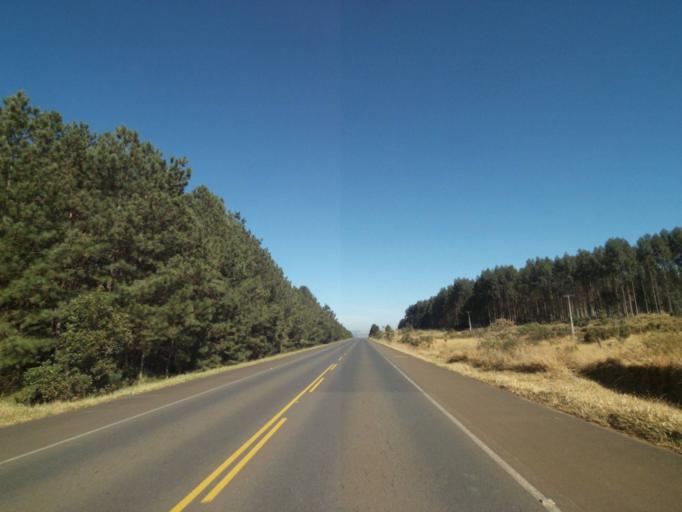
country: BR
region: Parana
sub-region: Tibagi
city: Tibagi
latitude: -24.4327
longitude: -50.4136
